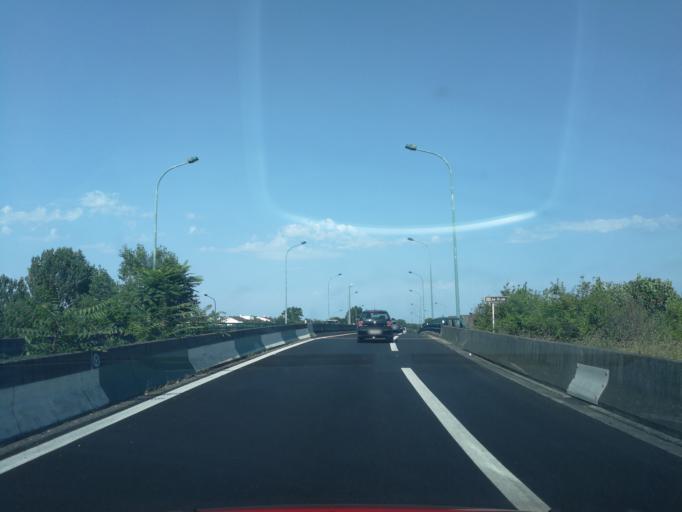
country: FR
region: Midi-Pyrenees
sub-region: Departement de la Haute-Garonne
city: Blagnac
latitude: 43.6203
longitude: 1.3928
